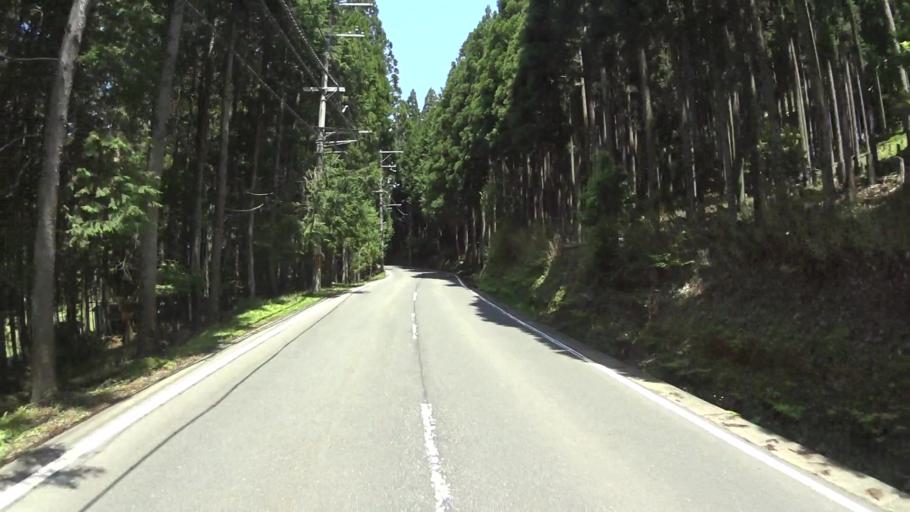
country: JP
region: Kyoto
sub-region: Kyoto-shi
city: Kamigyo-ku
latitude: 35.1923
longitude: 135.7055
